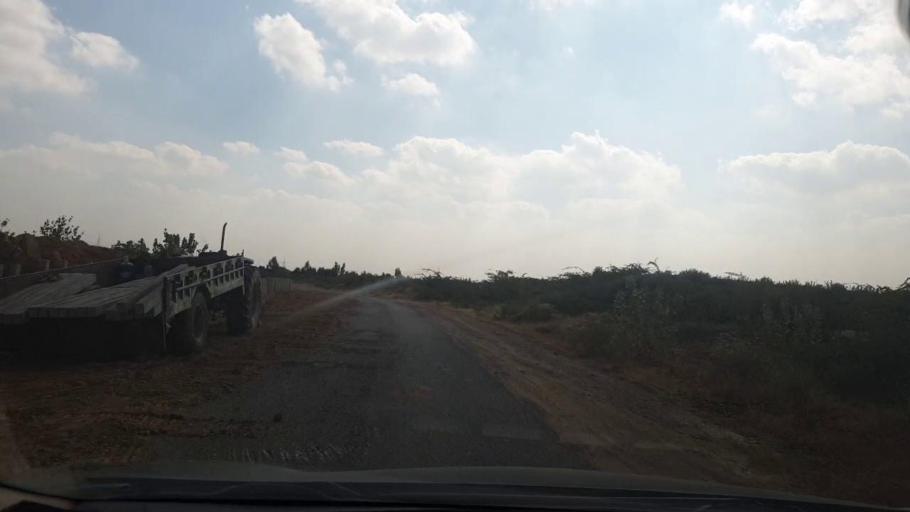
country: PK
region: Sindh
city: Malir Cantonment
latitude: 25.0240
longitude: 67.3532
